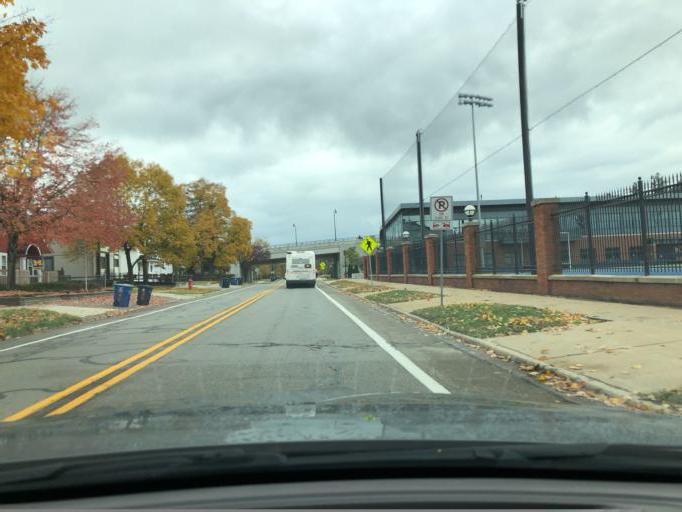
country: US
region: Michigan
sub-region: Washtenaw County
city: Ann Arbor
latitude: 42.2640
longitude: -83.7405
